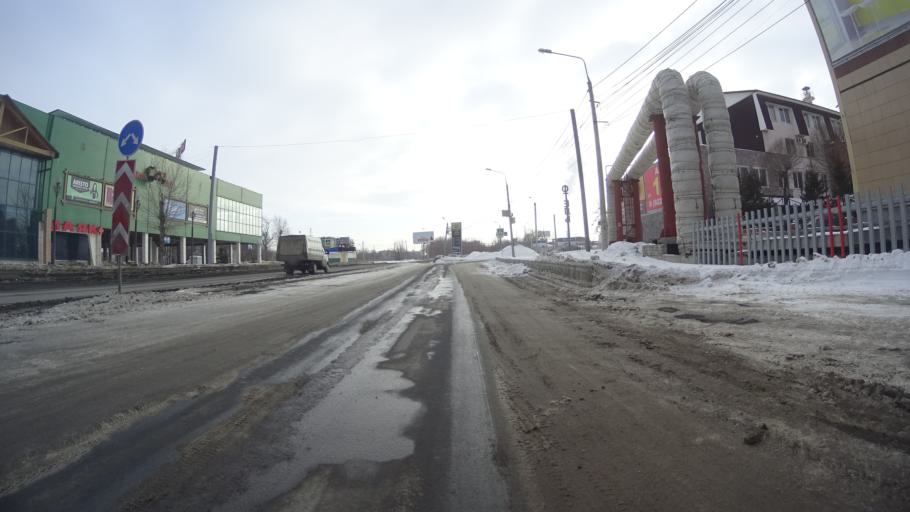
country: RU
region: Chelyabinsk
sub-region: Gorod Chelyabinsk
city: Chelyabinsk
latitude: 55.1191
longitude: 61.3862
